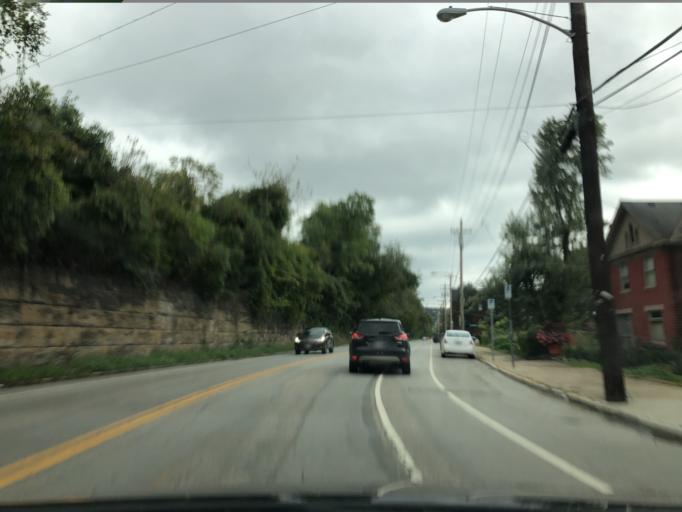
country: US
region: Kentucky
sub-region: Campbell County
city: Dayton
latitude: 39.1216
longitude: -84.4507
